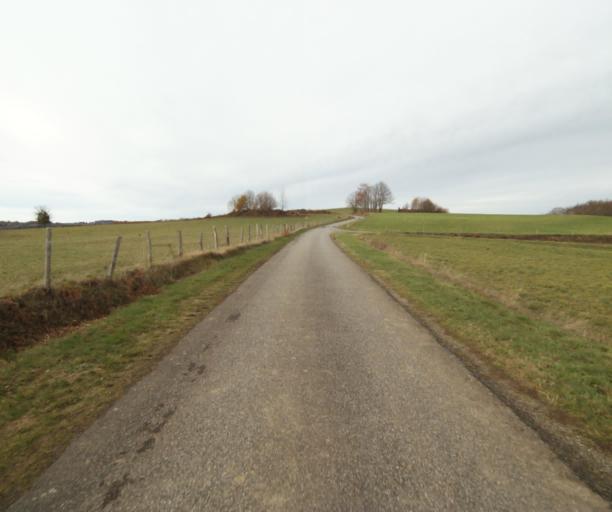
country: FR
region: Limousin
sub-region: Departement de la Correze
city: Sainte-Fortunade
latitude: 45.1620
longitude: 1.8099
